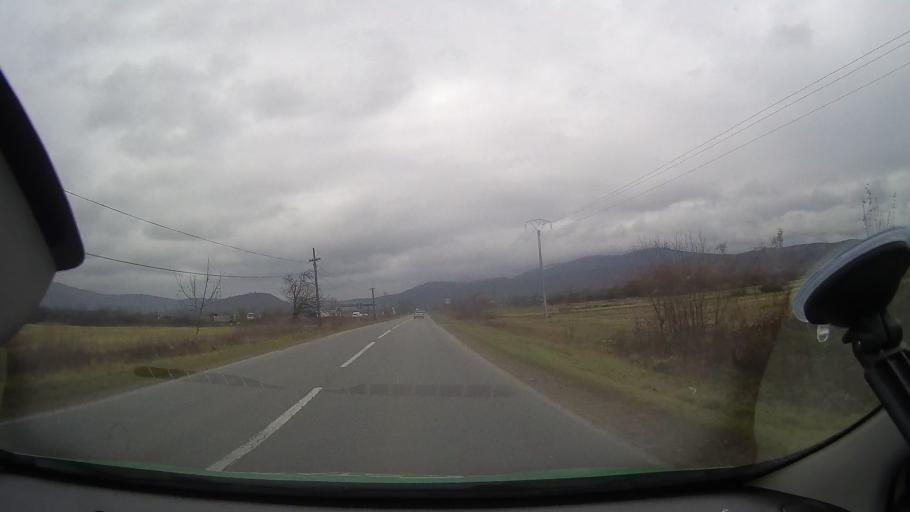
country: RO
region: Arad
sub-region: Comuna Buteni
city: Buteni
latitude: 46.3223
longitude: 22.1281
